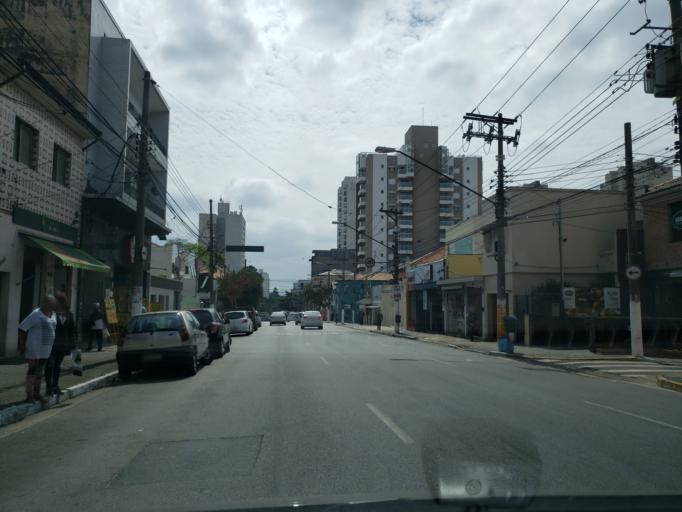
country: BR
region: Sao Paulo
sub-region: Sao Paulo
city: Sao Paulo
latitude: -23.5914
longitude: -46.6069
